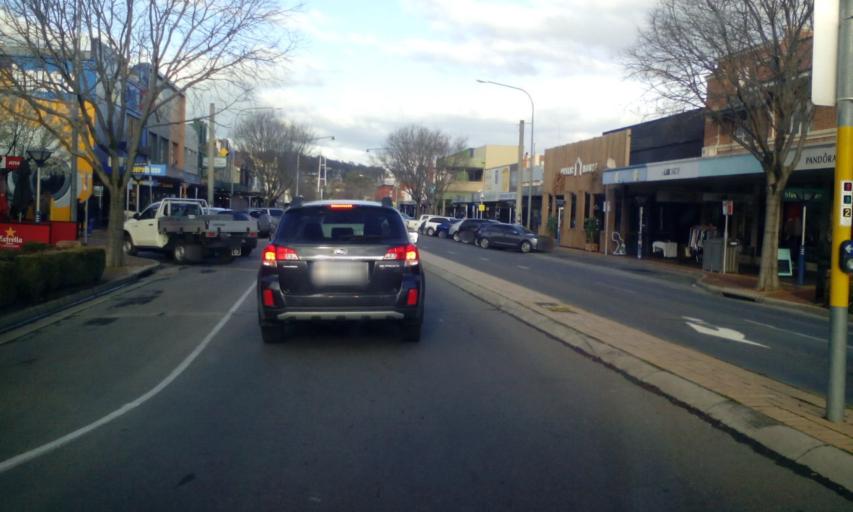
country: AU
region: New South Wales
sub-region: Albury Municipality
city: Albury
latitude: -36.0811
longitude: 146.9183
